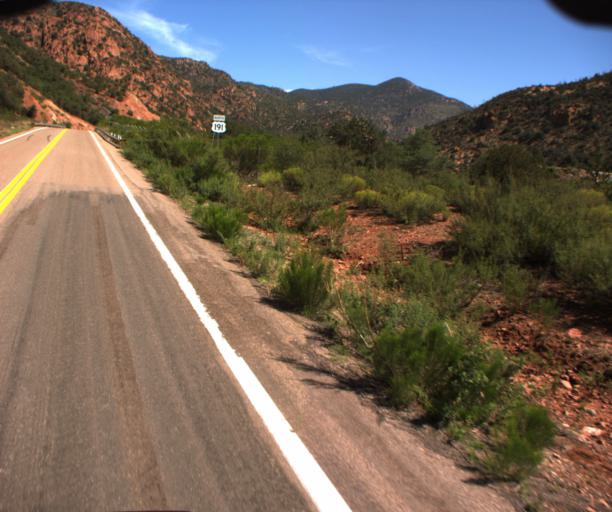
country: US
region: Arizona
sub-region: Greenlee County
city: Morenci
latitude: 33.1470
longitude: -109.3748
